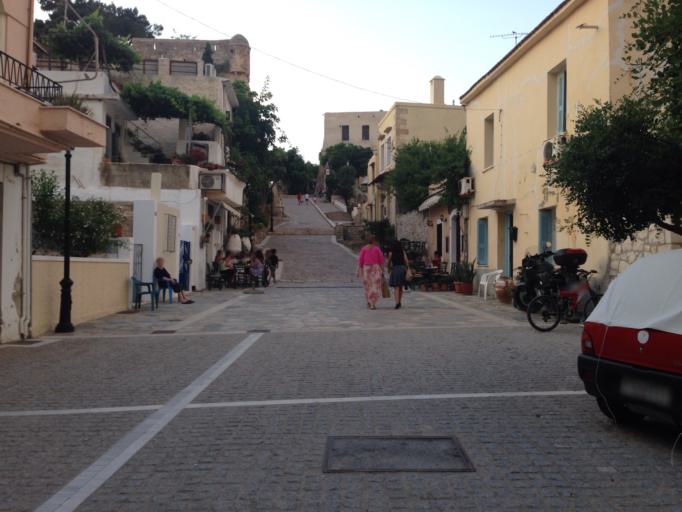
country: GR
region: Crete
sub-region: Nomos Rethymnis
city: Rethymno
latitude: 35.3708
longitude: 24.4727
